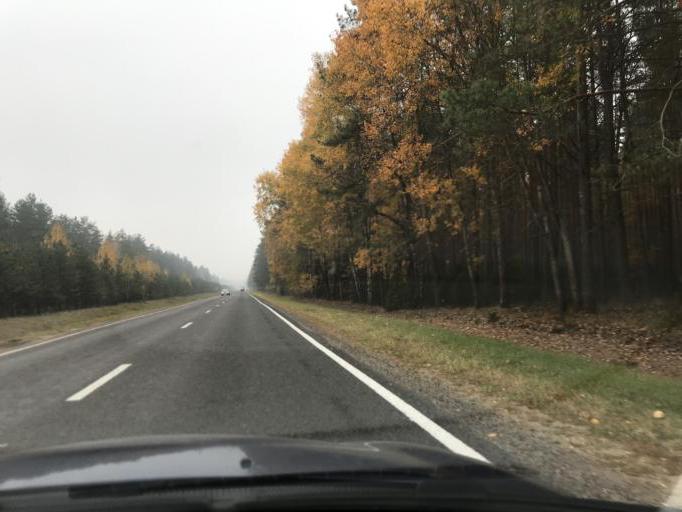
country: LT
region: Alytaus apskritis
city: Druskininkai
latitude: 53.9014
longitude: 23.9162
